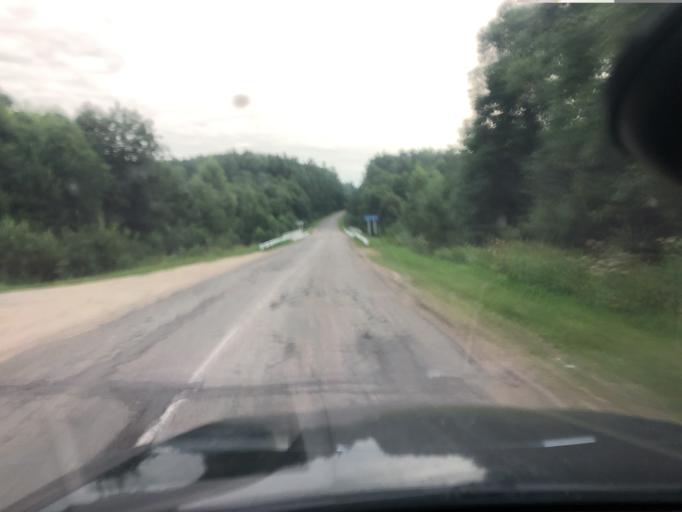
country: RU
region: Jaroslavl
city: Petrovsk
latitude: 56.9990
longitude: 39.0951
